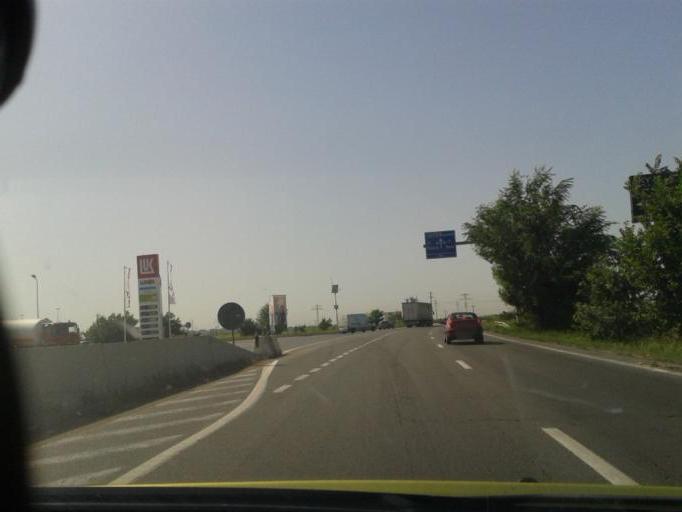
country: RO
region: Prahova
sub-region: Comuna Paulesti
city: Paulesti
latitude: 44.9649
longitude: 25.9642
